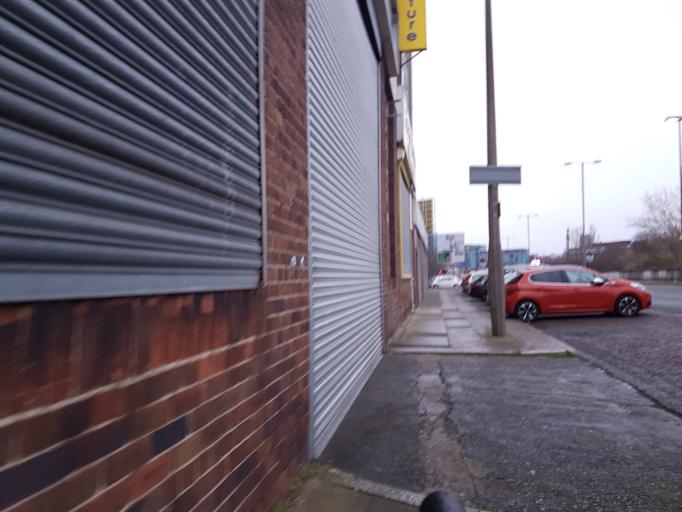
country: GB
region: England
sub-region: Liverpool
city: Liverpool
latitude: 53.4132
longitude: -2.9773
